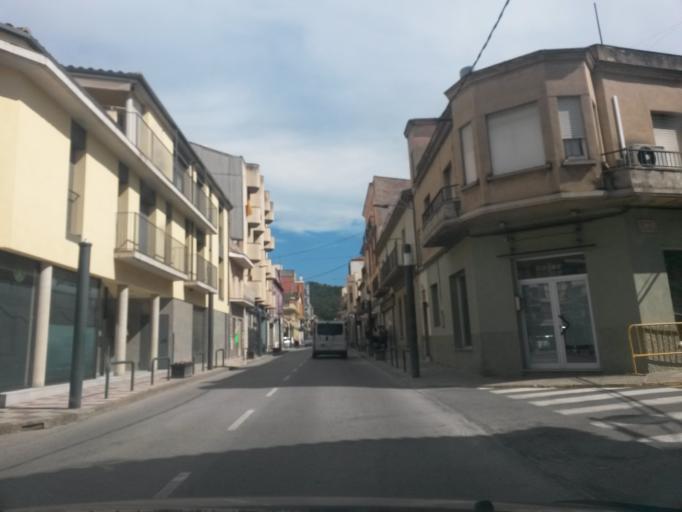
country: ES
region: Catalonia
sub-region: Provincia de Girona
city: Angles
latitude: 41.9570
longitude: 2.6362
